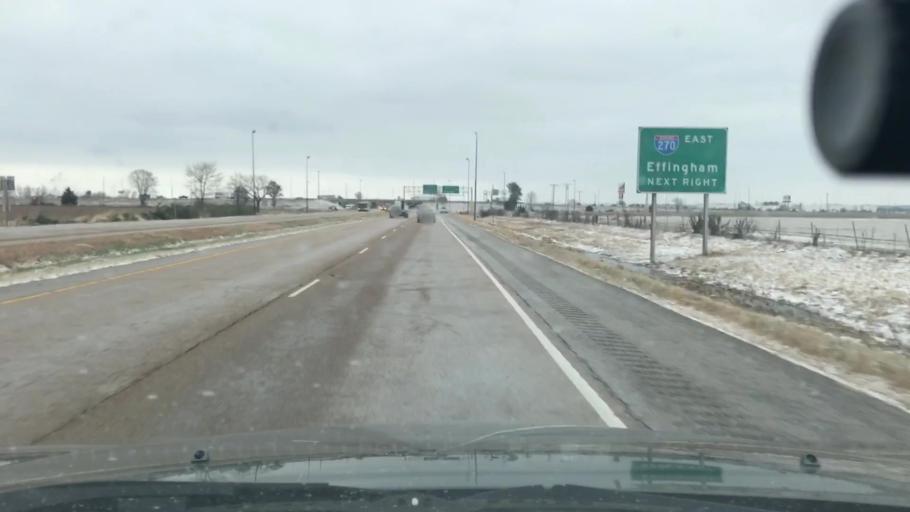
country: US
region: Illinois
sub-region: Madison County
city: Mitchell
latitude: 38.7526
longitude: -90.0694
